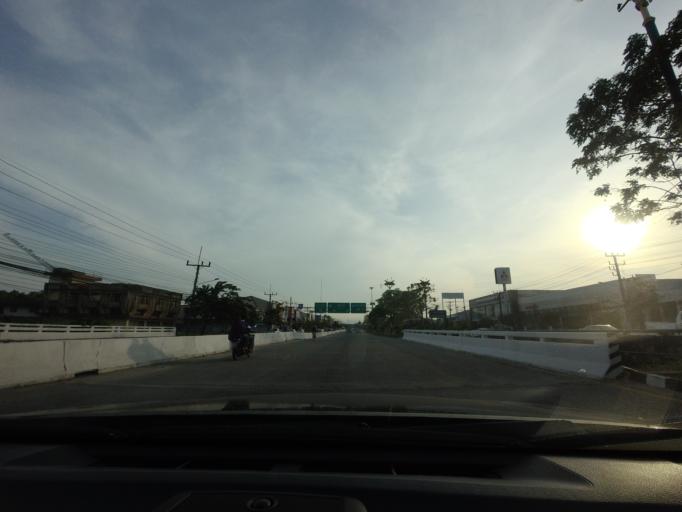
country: TH
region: Narathiwat
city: Narathiwat
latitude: 6.4176
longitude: 101.8137
